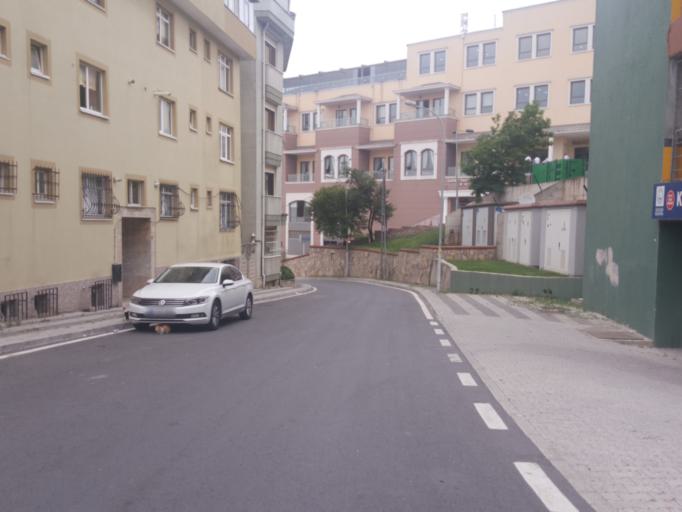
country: TR
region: Istanbul
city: UEskuedar
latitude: 41.0382
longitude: 29.0593
